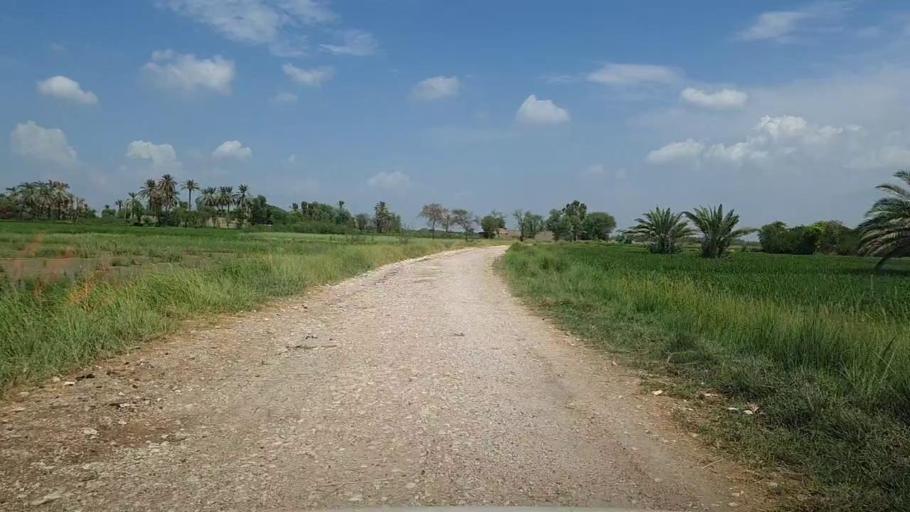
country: PK
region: Sindh
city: Bhiria
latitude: 26.9518
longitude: 68.2375
